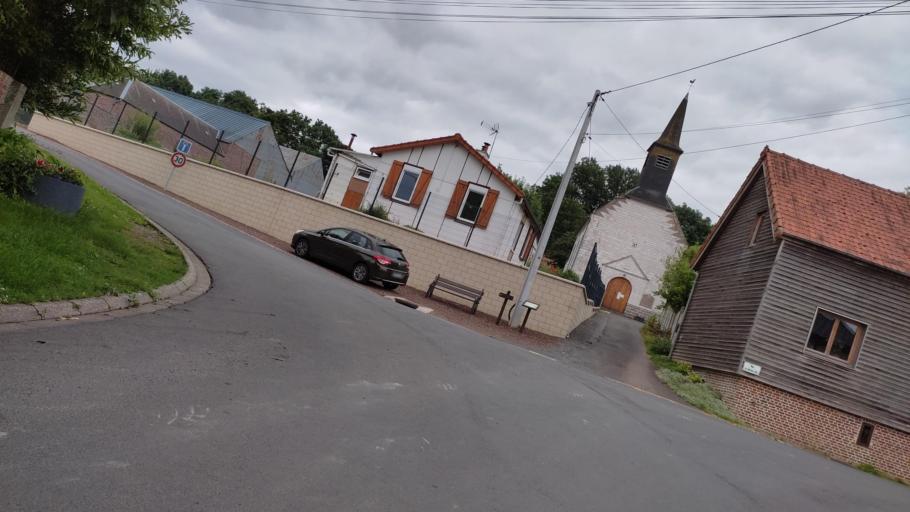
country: FR
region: Nord-Pas-de-Calais
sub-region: Departement du Pas-de-Calais
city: Beaumetz-les-Loges
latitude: 50.2393
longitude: 2.6287
